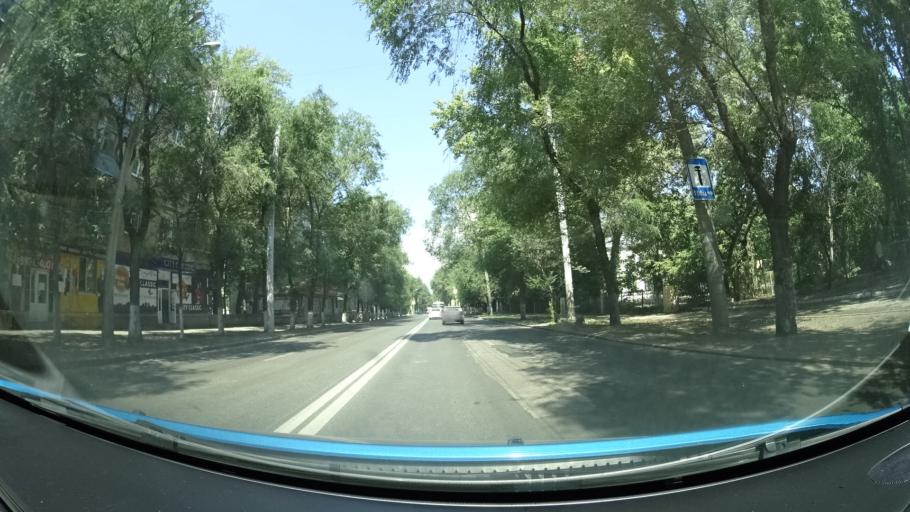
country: RU
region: Samara
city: Samara
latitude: 53.2061
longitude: 50.1621
